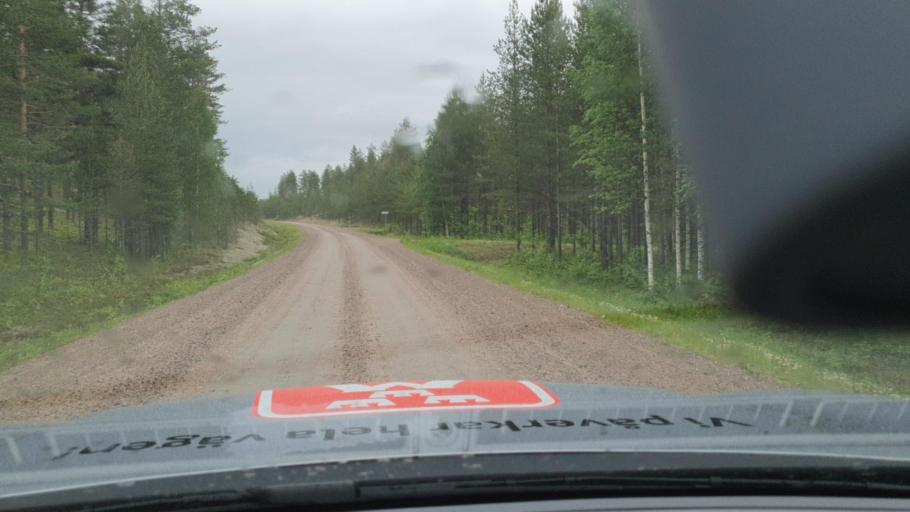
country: SE
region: Norrbotten
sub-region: Overkalix Kommun
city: OEverkalix
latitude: 66.5664
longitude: 22.7500
